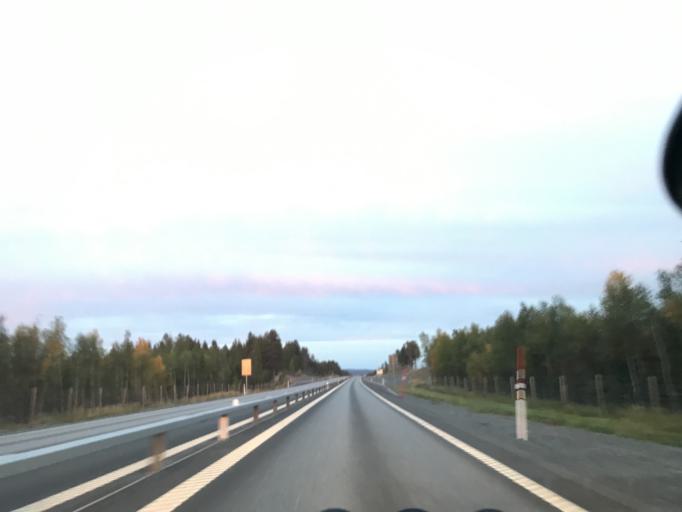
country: SE
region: Norrbotten
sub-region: Gallivare Kommun
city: Malmberget
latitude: 67.6854
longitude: 20.8582
